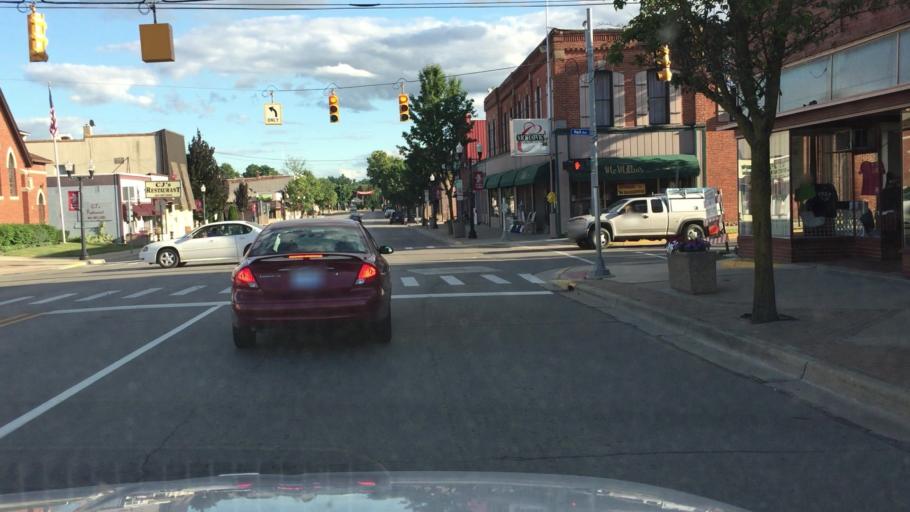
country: US
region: Michigan
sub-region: Saint Clair County
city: Yale
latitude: 43.1302
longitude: -82.7984
